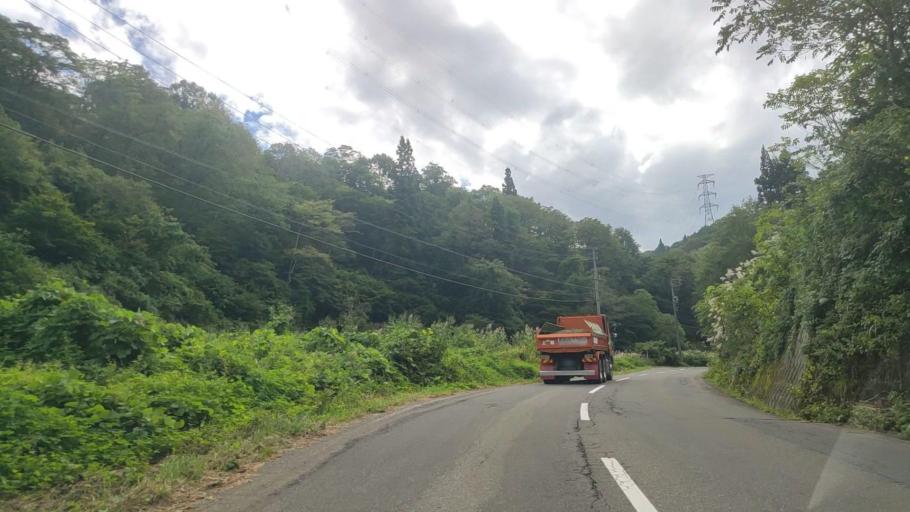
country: JP
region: Nagano
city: Iiyama
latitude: 36.8881
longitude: 138.3230
